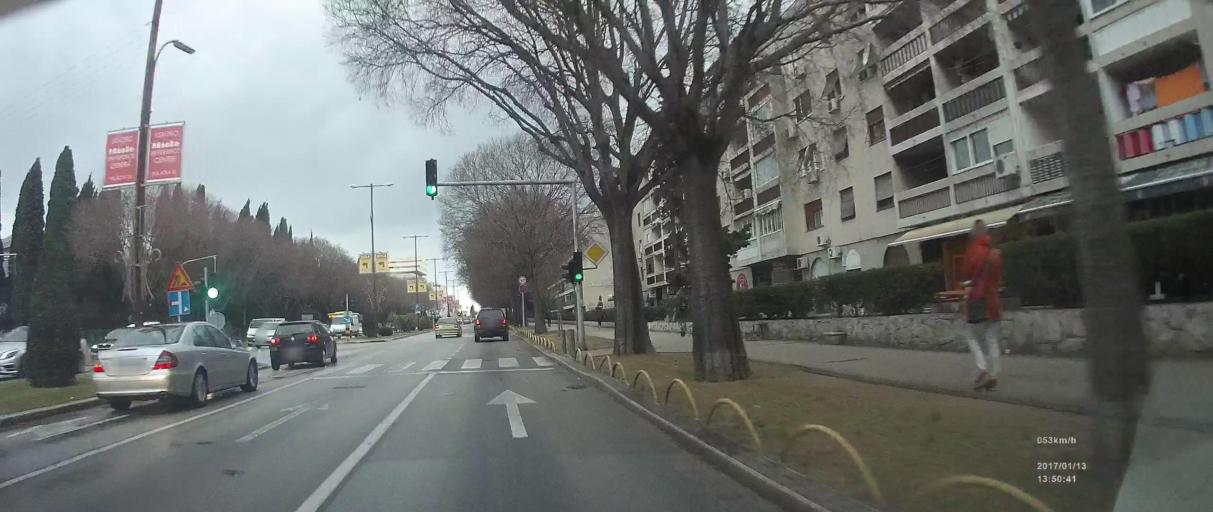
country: HR
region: Splitsko-Dalmatinska
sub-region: Grad Split
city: Split
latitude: 43.5060
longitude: 16.4604
